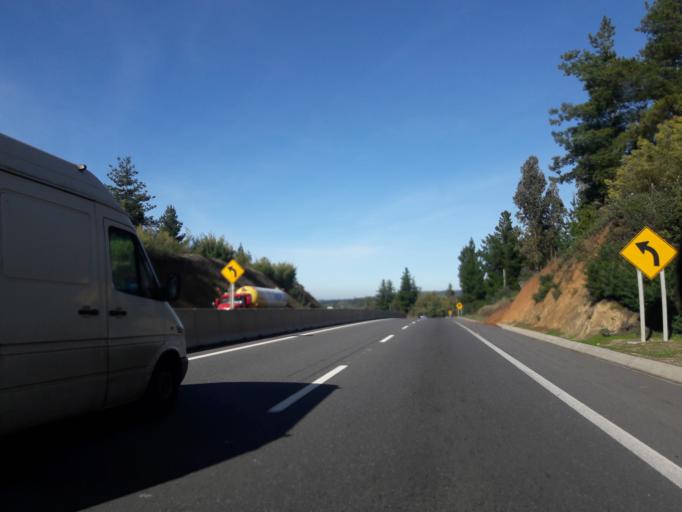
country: CL
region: Biobio
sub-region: Provincia de Biobio
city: Yumbel
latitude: -36.9757
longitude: -72.6523
